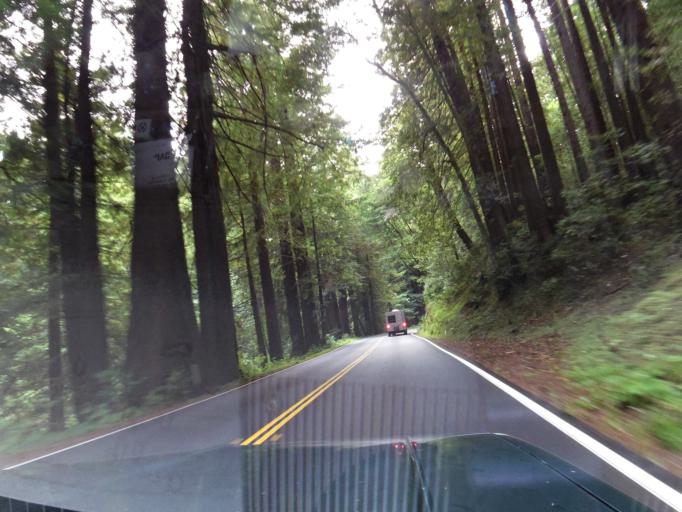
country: US
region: California
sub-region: Mendocino County
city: Fort Bragg
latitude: 39.1773
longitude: -123.6908
